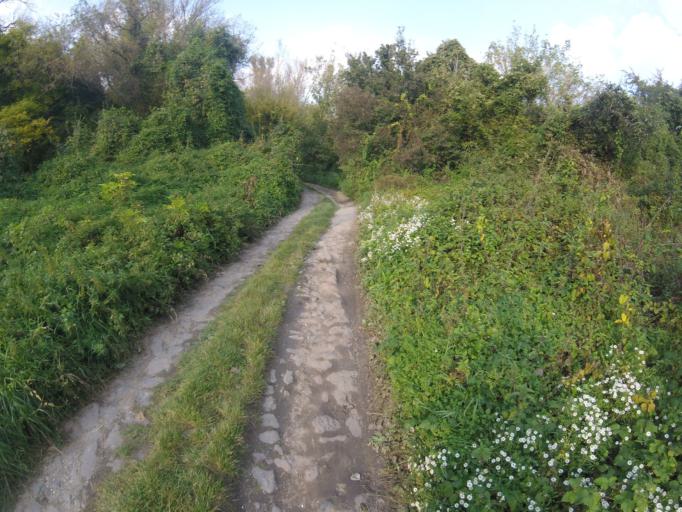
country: HU
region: Pest
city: Szob
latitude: 47.8098
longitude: 18.8466
